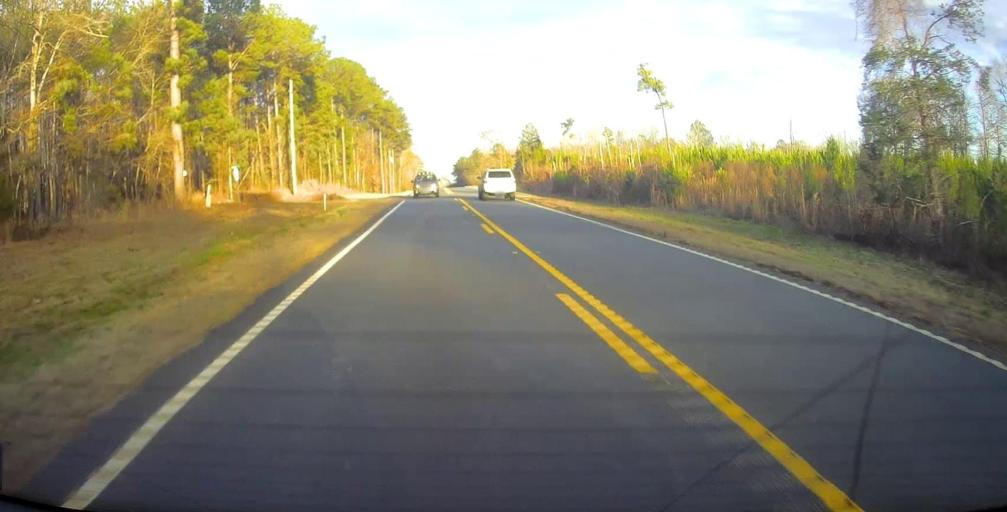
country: US
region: Georgia
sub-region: Talbot County
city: Sardis
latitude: 32.7197
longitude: -84.6696
